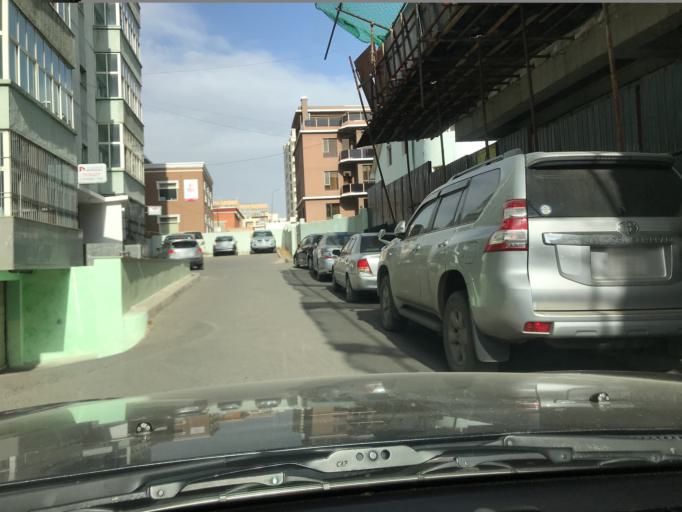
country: MN
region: Ulaanbaatar
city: Ulaanbaatar
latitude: 47.9195
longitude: 106.9392
